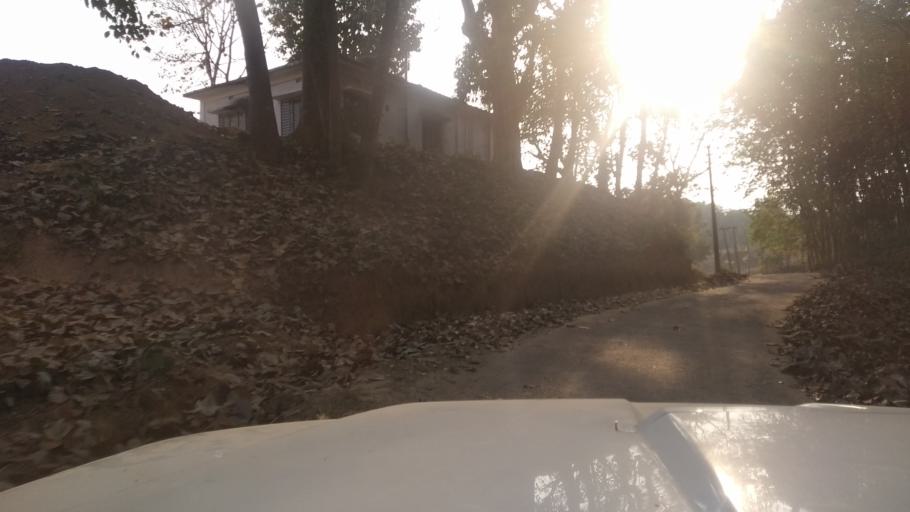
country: IN
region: Tripura
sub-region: West Tripura
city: Sonamura
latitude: 23.3495
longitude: 91.3234
